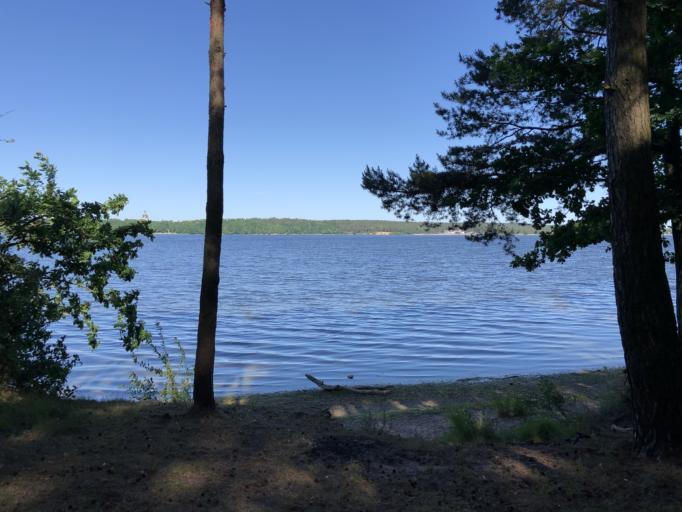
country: LT
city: Ramuciai
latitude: 54.8763
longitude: 24.0496
